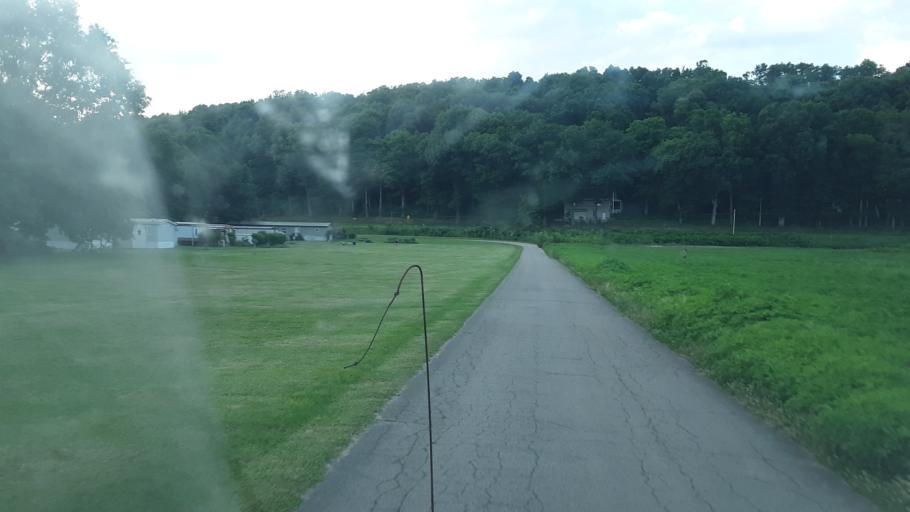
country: US
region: Ohio
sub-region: Sandusky County
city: Bellville
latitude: 40.6056
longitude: -82.4621
